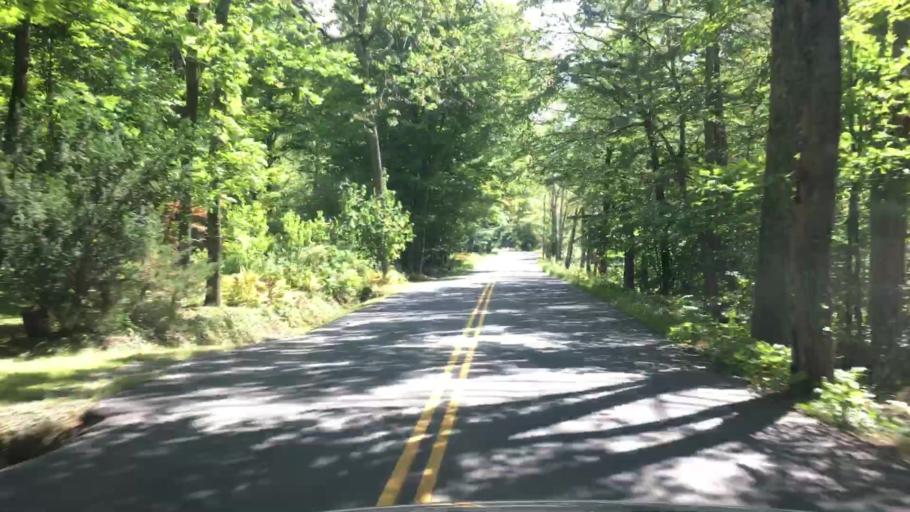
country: US
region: Vermont
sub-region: Windham County
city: West Brattleboro
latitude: 42.8041
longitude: -72.6969
